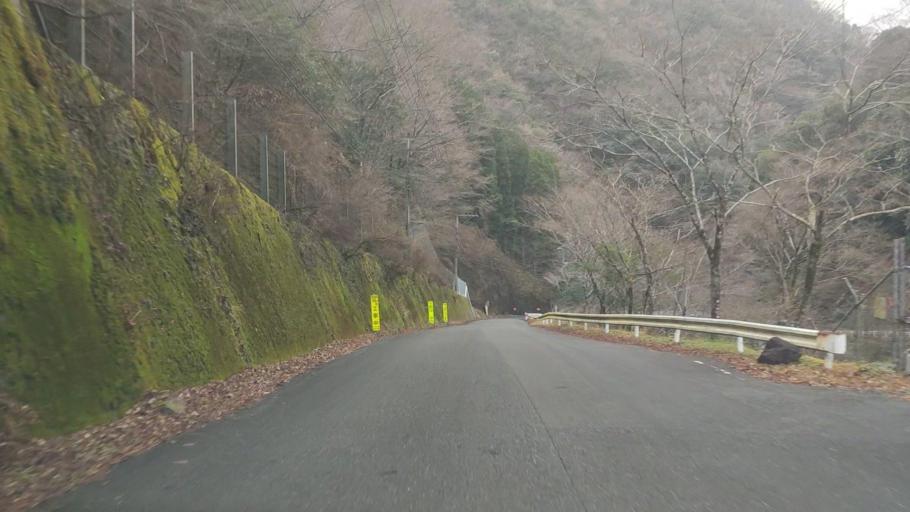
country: JP
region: Kumamoto
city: Matsubase
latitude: 32.4848
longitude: 130.8941
